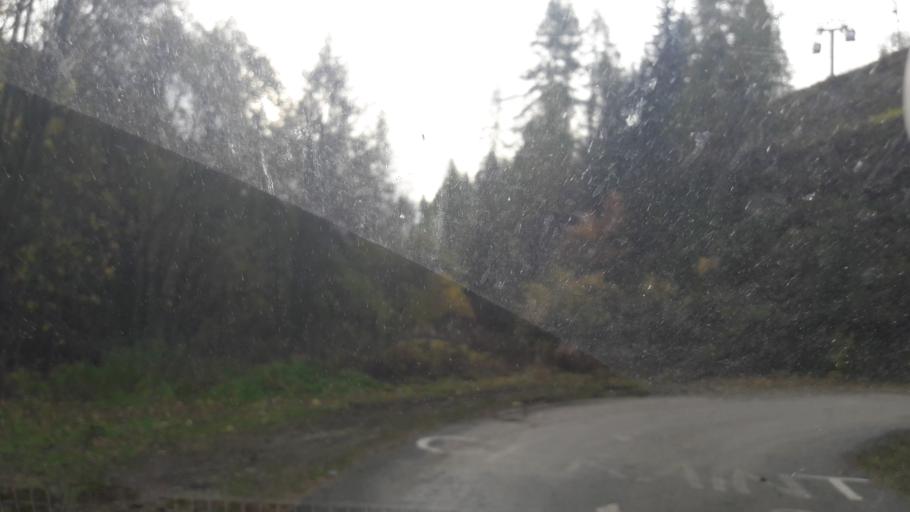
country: FR
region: Rhone-Alpes
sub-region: Departement de la Savoie
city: Tignes
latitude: 45.5036
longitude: 6.9219
